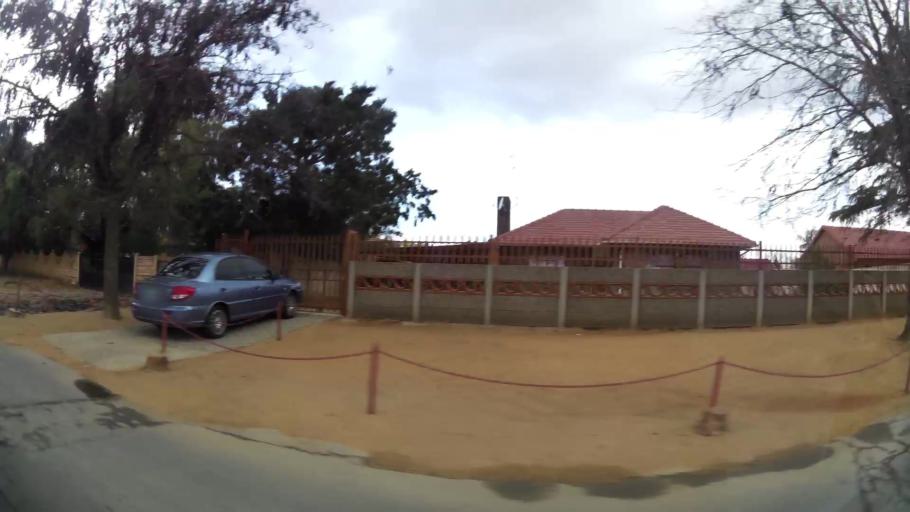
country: ZA
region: Orange Free State
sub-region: Lejweleputswa District Municipality
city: Welkom
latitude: -27.9676
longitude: 26.7244
